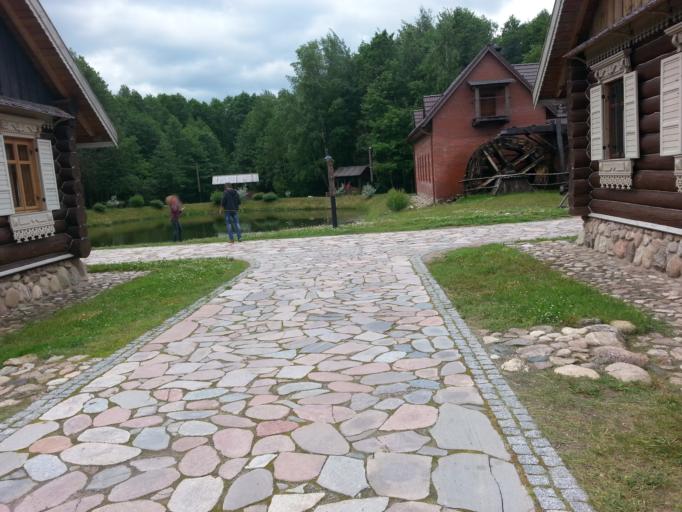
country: BY
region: Minsk
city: Narach
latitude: 54.8609
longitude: 26.7103
